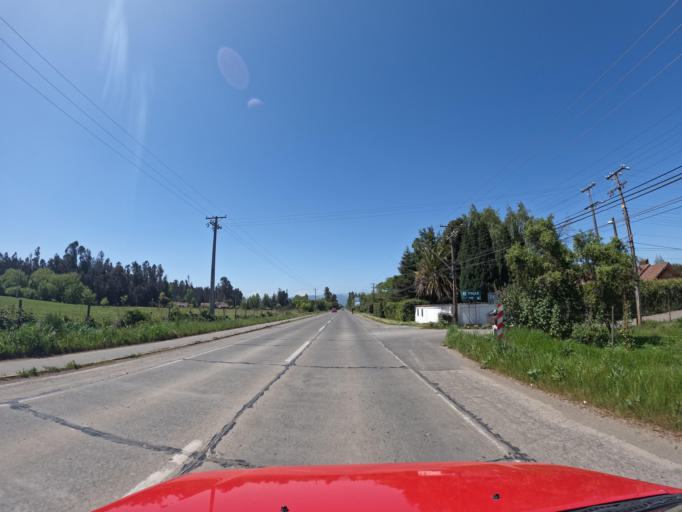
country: CL
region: Maule
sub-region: Provincia de Linares
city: Linares
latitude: -35.8345
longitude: -71.5457
